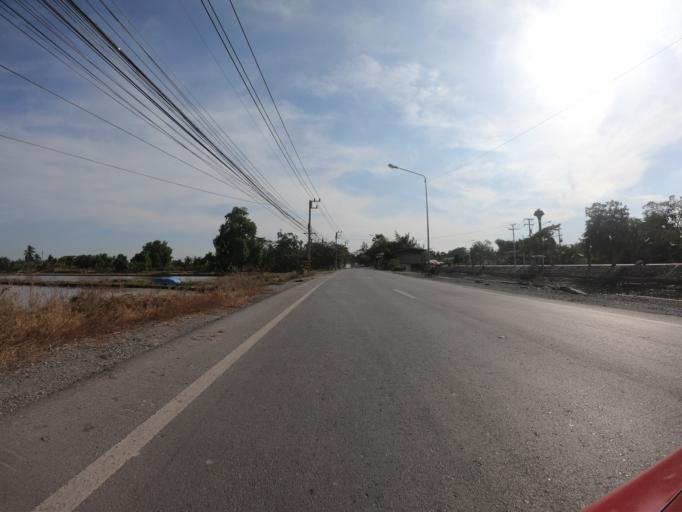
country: TH
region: Pathum Thani
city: Thanyaburi
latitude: 13.9965
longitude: 100.7305
